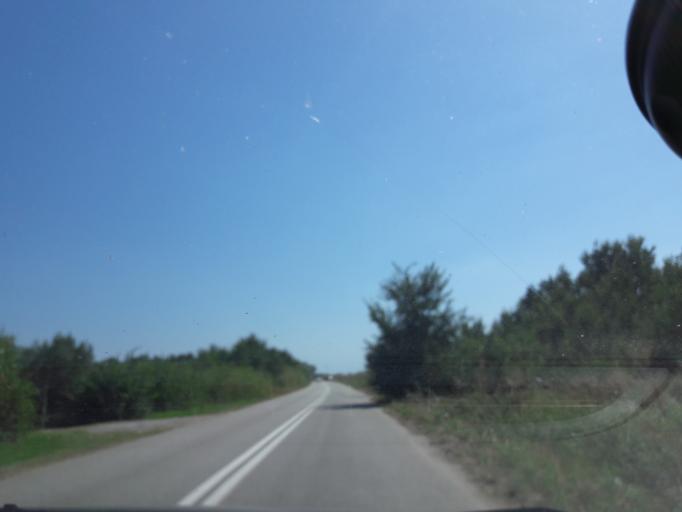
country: GR
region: Central Macedonia
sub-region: Nomos Chalkidikis
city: Nea Kallikrateia
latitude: 40.3294
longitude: 23.0236
